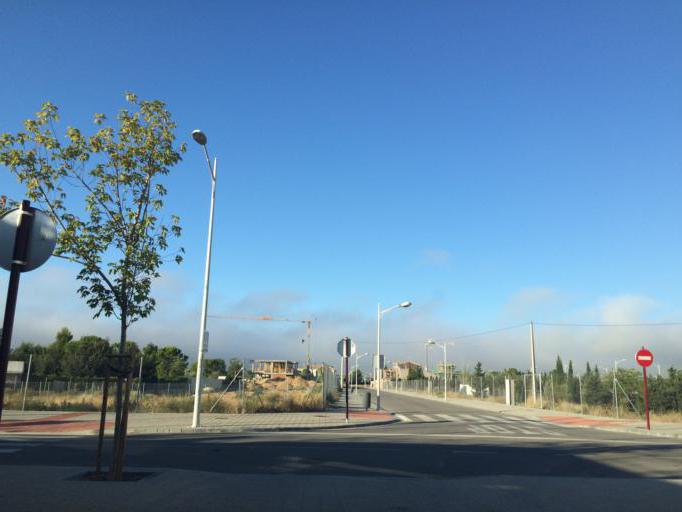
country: ES
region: Castille-La Mancha
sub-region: Provincia de Albacete
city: Albacete
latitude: 39.0054
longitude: -1.8796
